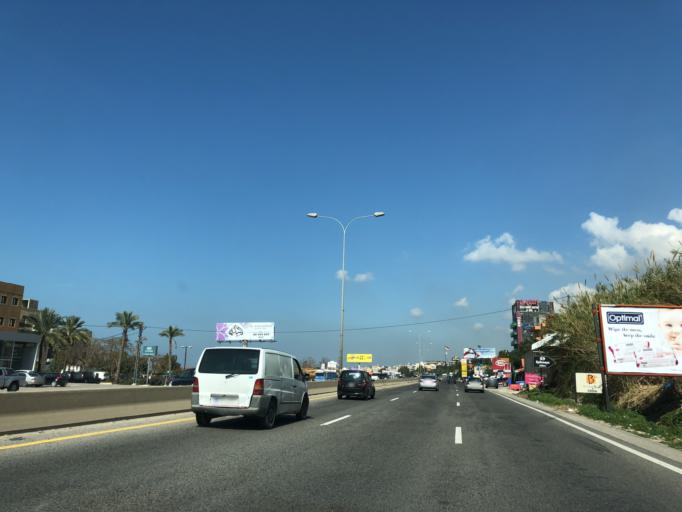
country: LB
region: Mont-Liban
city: Jbail
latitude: 34.1073
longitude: 35.6534
